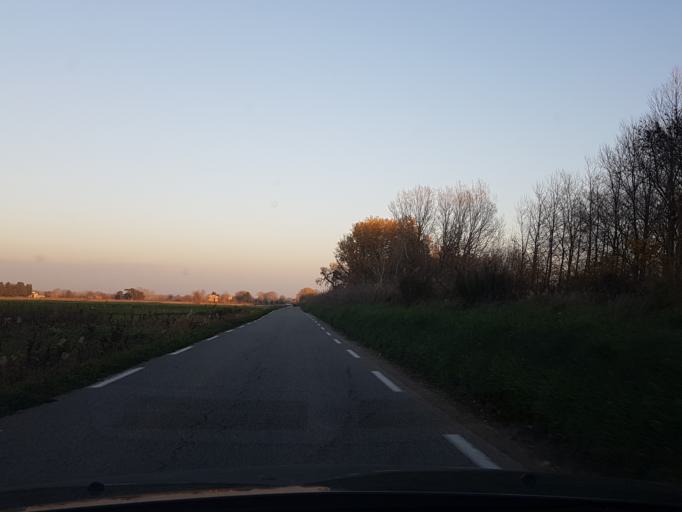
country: FR
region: Provence-Alpes-Cote d'Azur
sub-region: Departement du Vaucluse
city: Bedarrides
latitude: 44.0316
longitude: 4.9257
